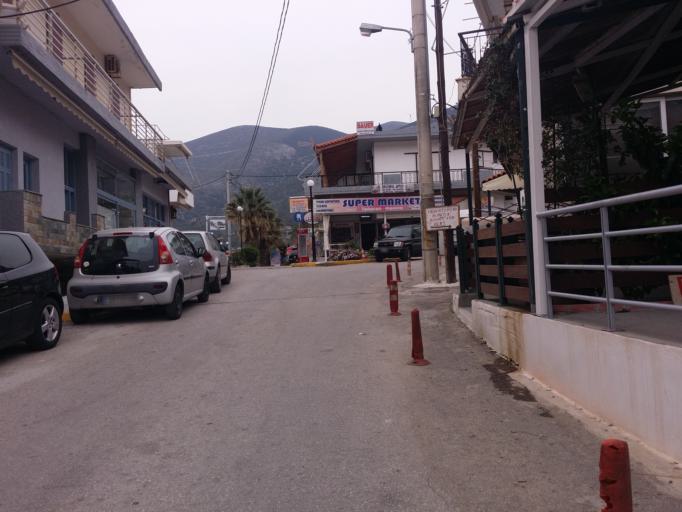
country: GR
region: Central Greece
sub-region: Nomos Voiotias
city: Kaparellion
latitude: 38.1505
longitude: 23.2257
